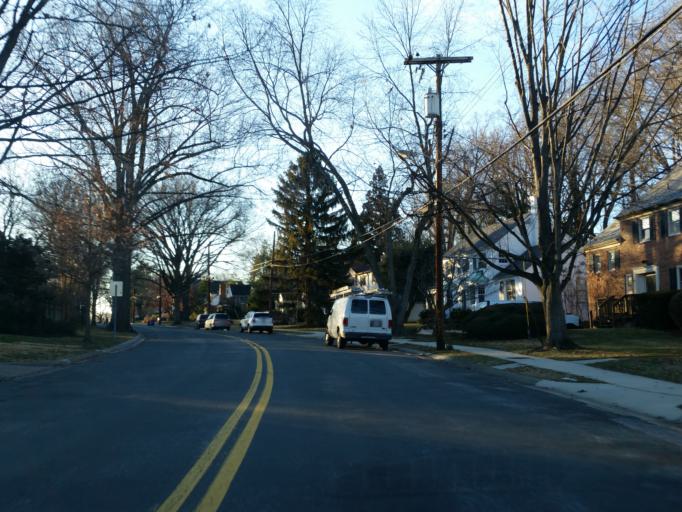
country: US
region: Maryland
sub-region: Montgomery County
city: Bethesda
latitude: 38.9694
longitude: -77.1133
